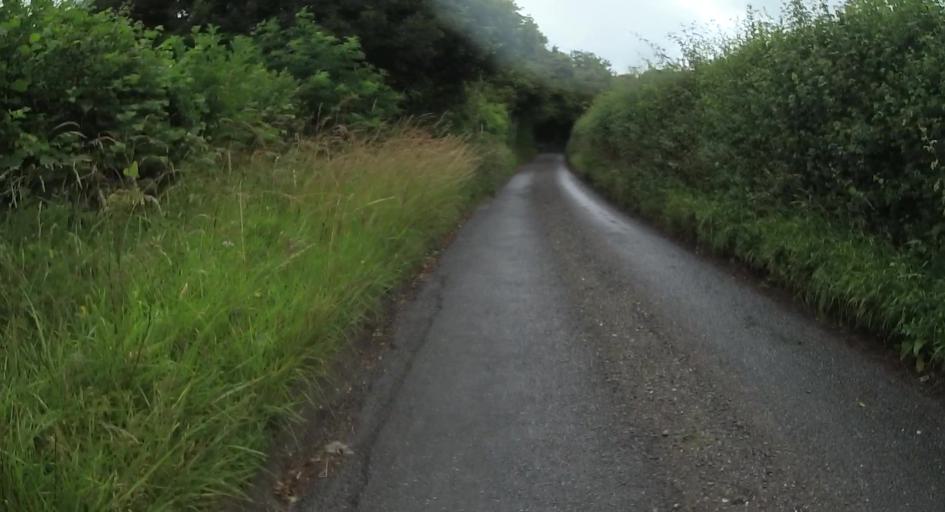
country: GB
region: England
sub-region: Hampshire
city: Long Sutton
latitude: 51.1967
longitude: -0.9137
